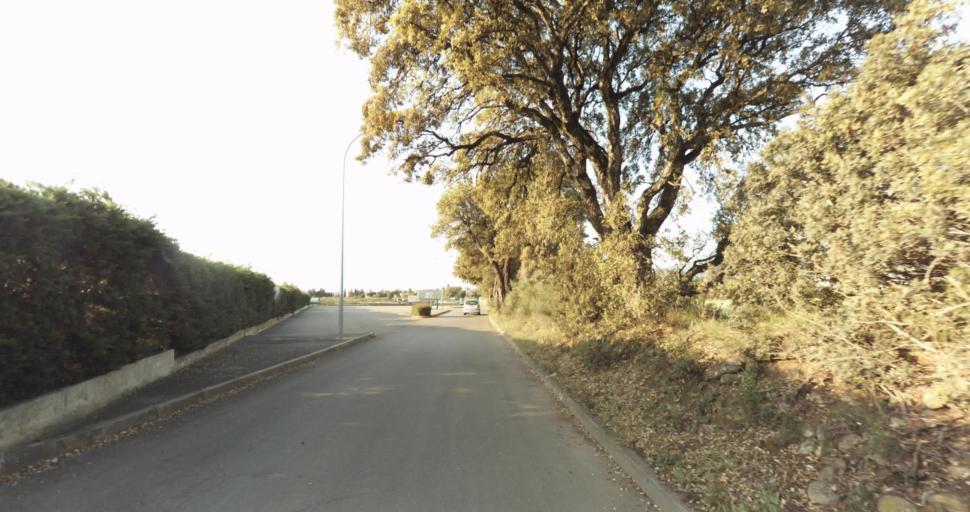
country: FR
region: Corsica
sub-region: Departement de la Haute-Corse
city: Biguglia
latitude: 42.6083
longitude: 9.4439
